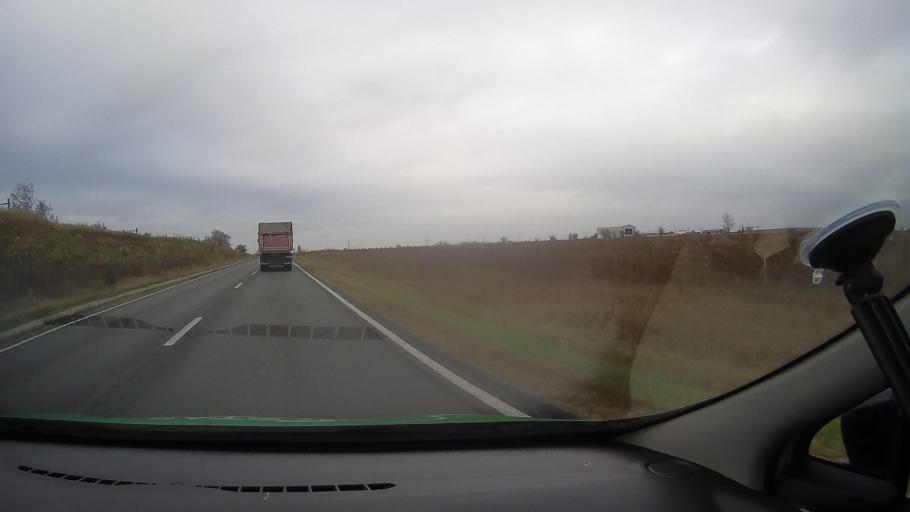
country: RO
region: Constanta
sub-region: Comuna Poarta Alba
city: Poarta Alba
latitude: 44.2282
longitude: 28.3805
